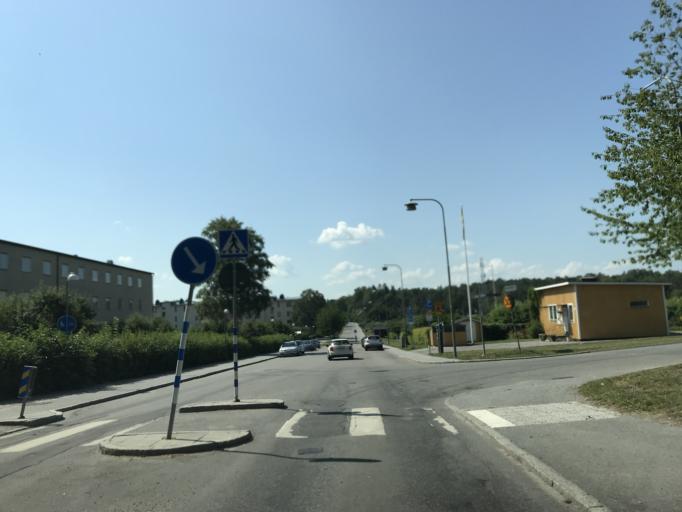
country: SE
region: Stockholm
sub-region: Stockholms Kommun
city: Bromma
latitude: 59.3322
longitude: 17.9603
